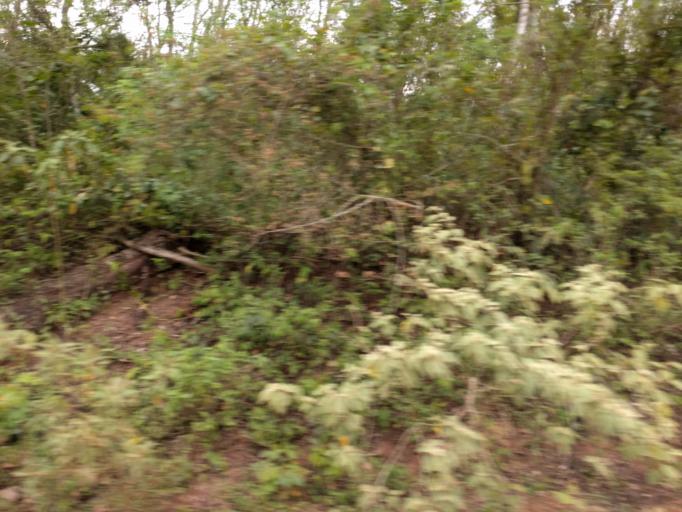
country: BO
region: Santa Cruz
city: Santiago del Torno
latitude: -17.9204
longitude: -63.4247
